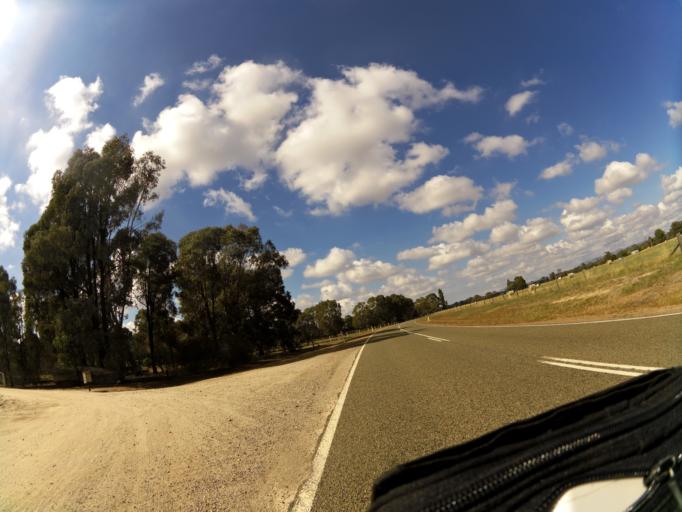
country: AU
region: Victoria
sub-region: Benalla
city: Benalla
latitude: -36.5831
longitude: 146.0083
